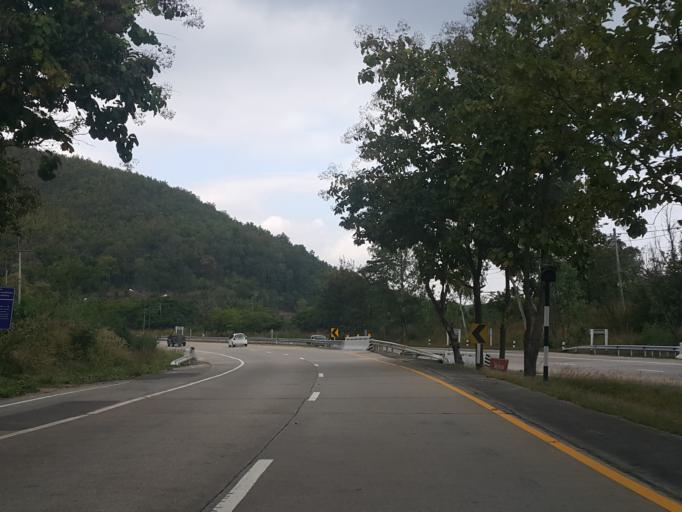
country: TH
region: Lamphun
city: Mae Tha
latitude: 18.5093
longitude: 99.1287
